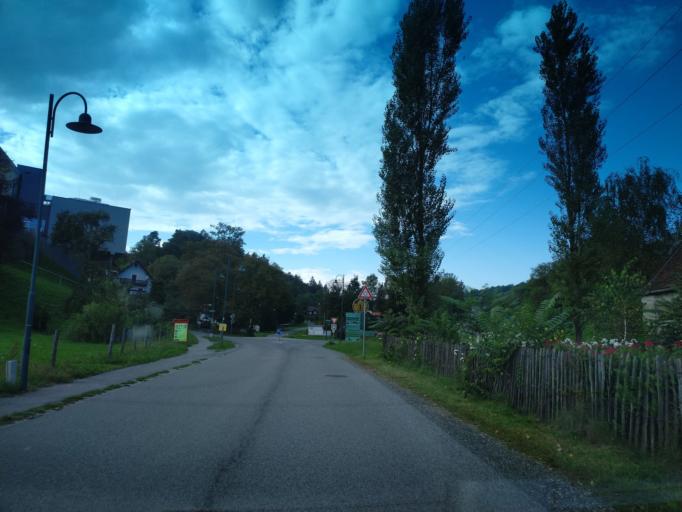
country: AT
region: Styria
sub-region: Politischer Bezirk Leibnitz
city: Kaindorf an der Sulm
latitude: 46.7952
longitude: 15.5266
